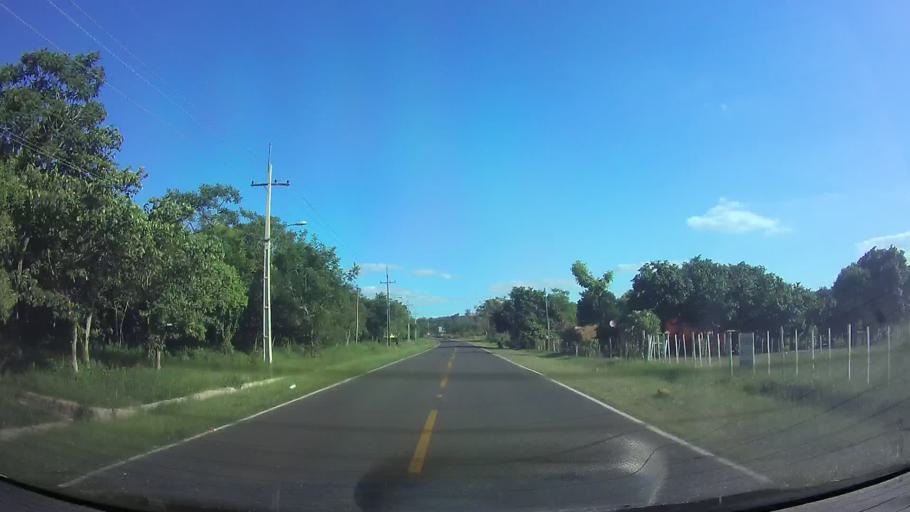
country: PY
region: Cordillera
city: Atyra
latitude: -25.2983
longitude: -57.1620
